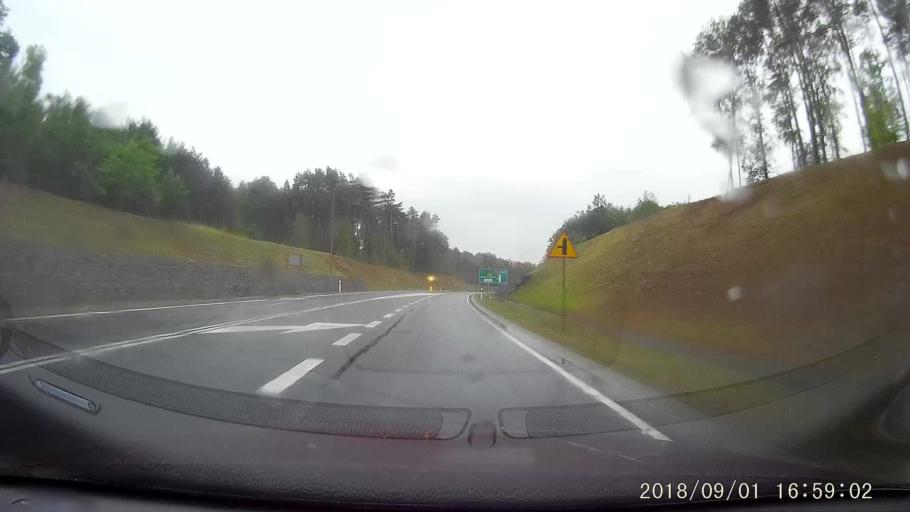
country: PL
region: Lubusz
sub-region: Powiat zielonogorski
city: Swidnica
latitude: 51.9115
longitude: 15.4206
